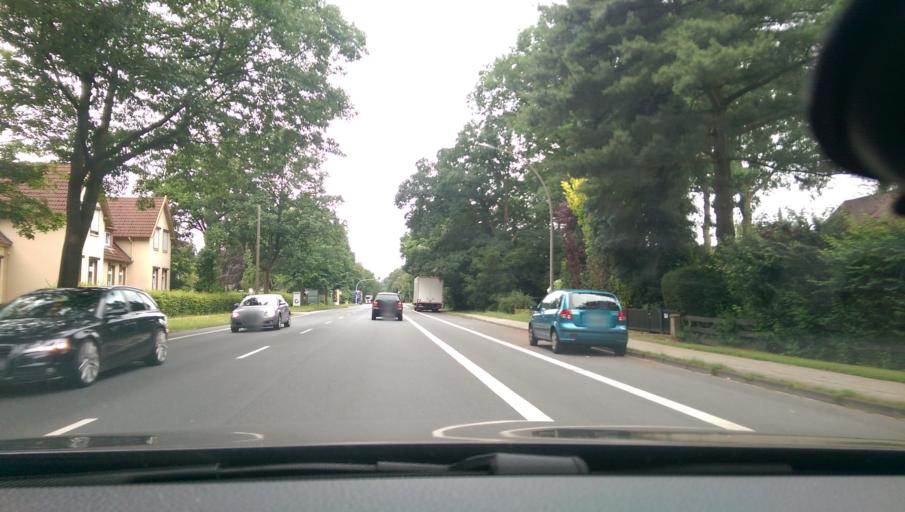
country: DE
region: Lower Saxony
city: Rotenburg
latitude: 53.1009
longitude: 9.3876
